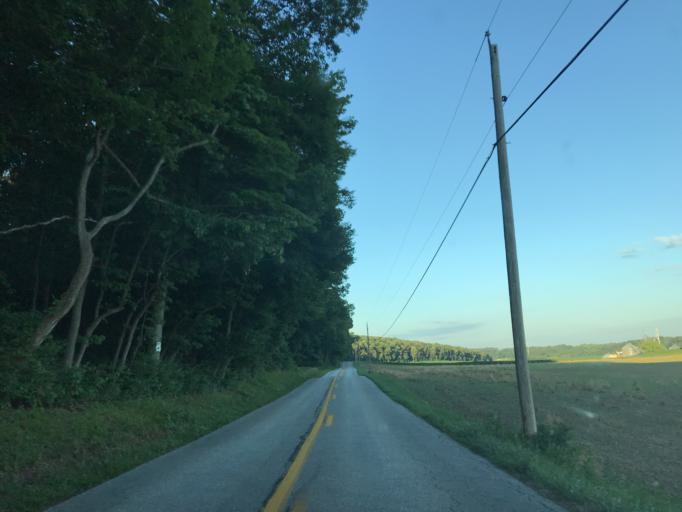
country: US
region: Maryland
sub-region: Baltimore County
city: Hunt Valley
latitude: 39.5657
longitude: -76.6869
